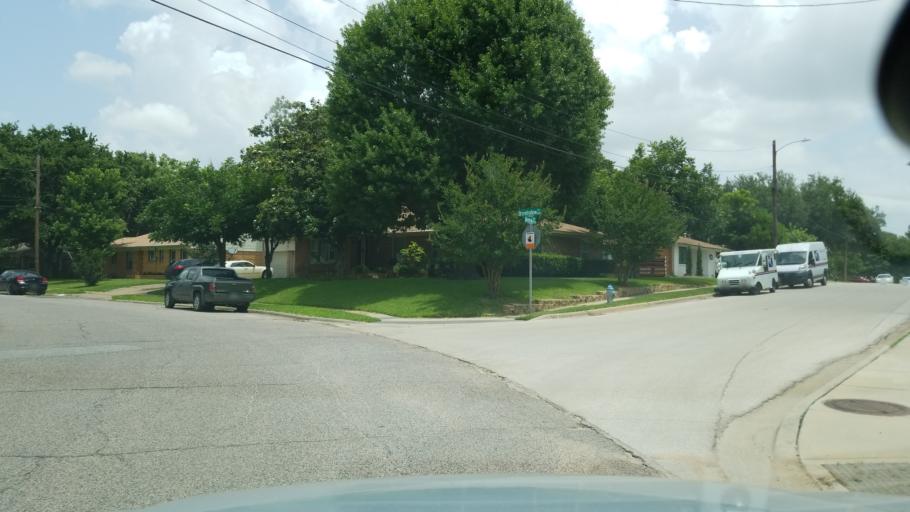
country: US
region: Texas
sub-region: Dallas County
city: Irving
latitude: 32.8288
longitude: -96.9230
